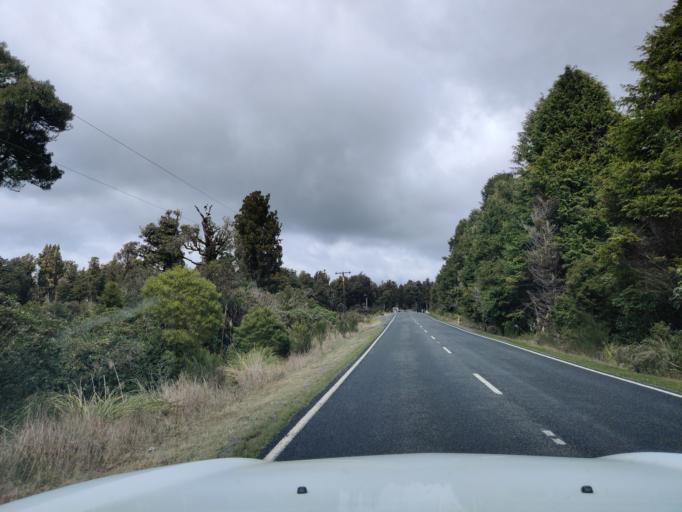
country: NZ
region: Manawatu-Wanganui
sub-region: Ruapehu District
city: Waiouru
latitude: -39.2402
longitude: 175.3917
